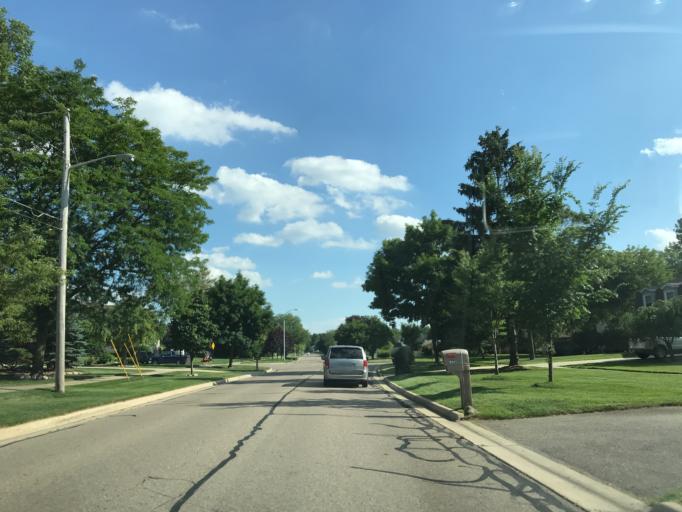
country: US
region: Michigan
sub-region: Oakland County
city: Farmington
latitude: 42.4193
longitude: -83.3942
